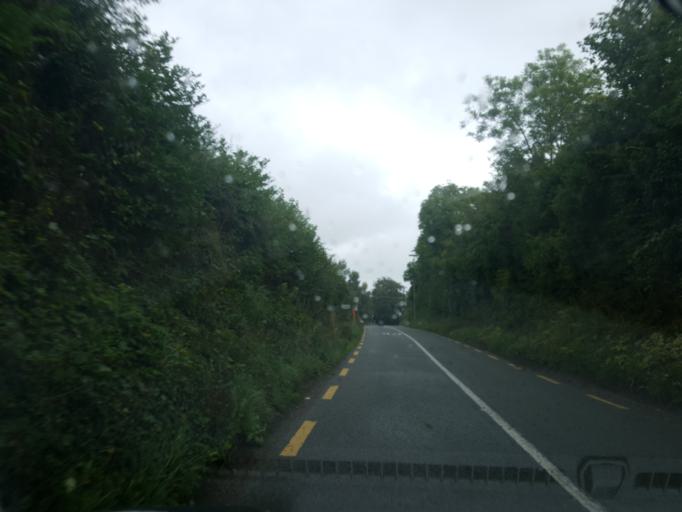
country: IE
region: Leinster
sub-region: Wicklow
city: Valleymount
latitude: 53.1235
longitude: -6.6312
